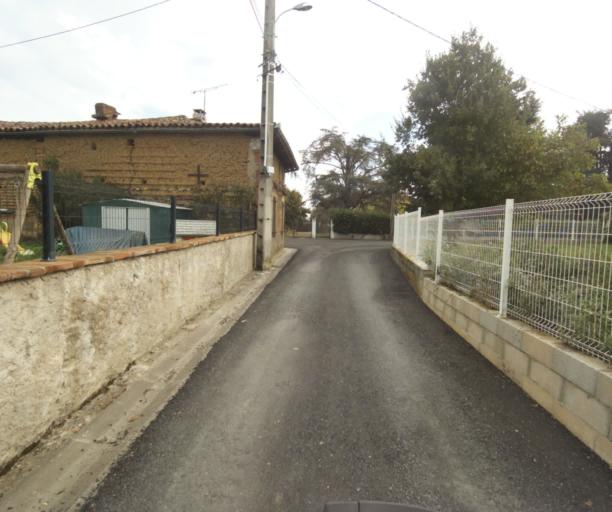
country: FR
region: Midi-Pyrenees
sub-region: Departement du Tarn-et-Garonne
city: Finhan
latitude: 43.9121
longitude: 1.2219
